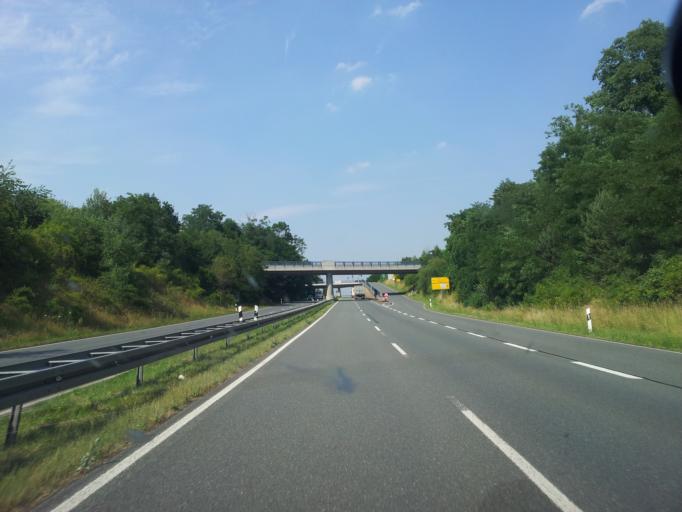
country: DE
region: Saxony
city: Riesa
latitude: 51.3016
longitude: 13.2833
